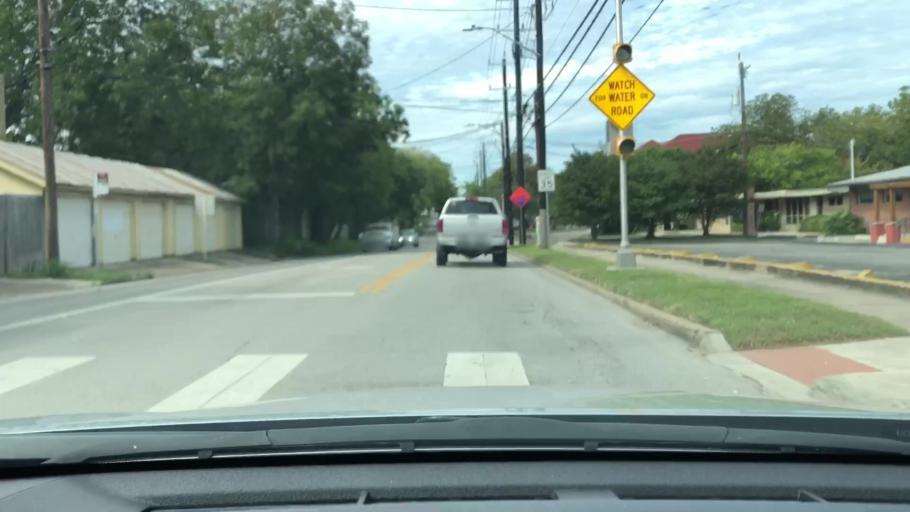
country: US
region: Texas
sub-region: Bexar County
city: Olmos Park
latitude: 29.4665
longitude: -98.4871
